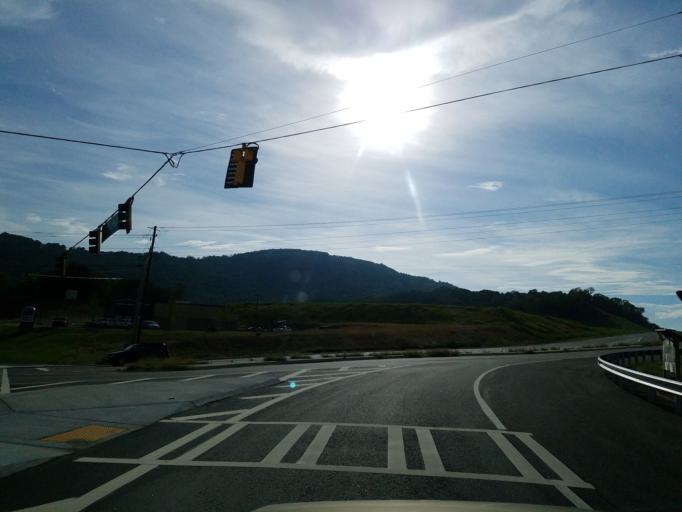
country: US
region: Georgia
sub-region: White County
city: Cleveland
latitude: 34.5792
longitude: -83.7634
